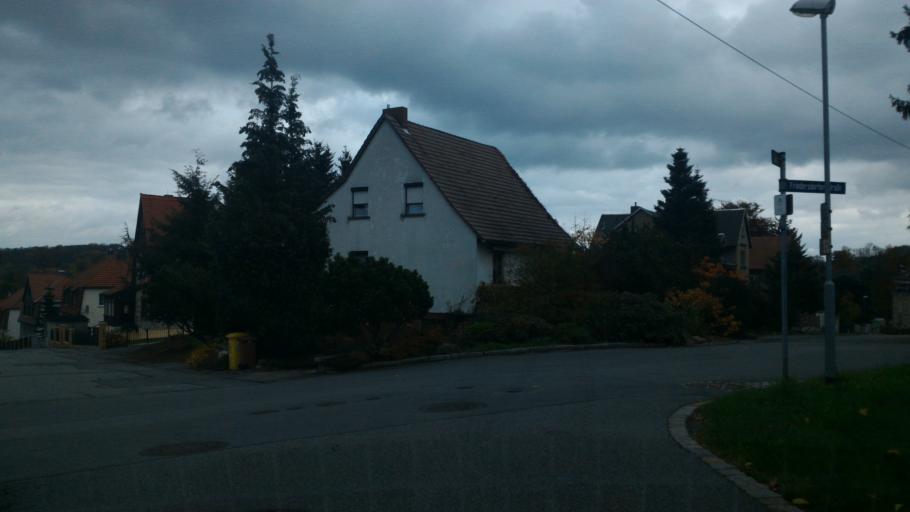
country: DE
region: Saxony
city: Ebersbach
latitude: 51.0087
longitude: 14.5724
